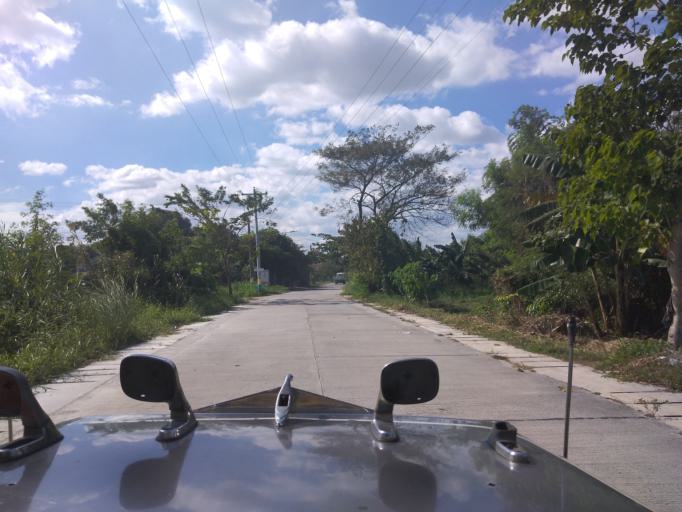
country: PH
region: Central Luzon
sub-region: Province of Pampanga
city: Magliman
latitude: 15.0288
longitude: 120.6317
